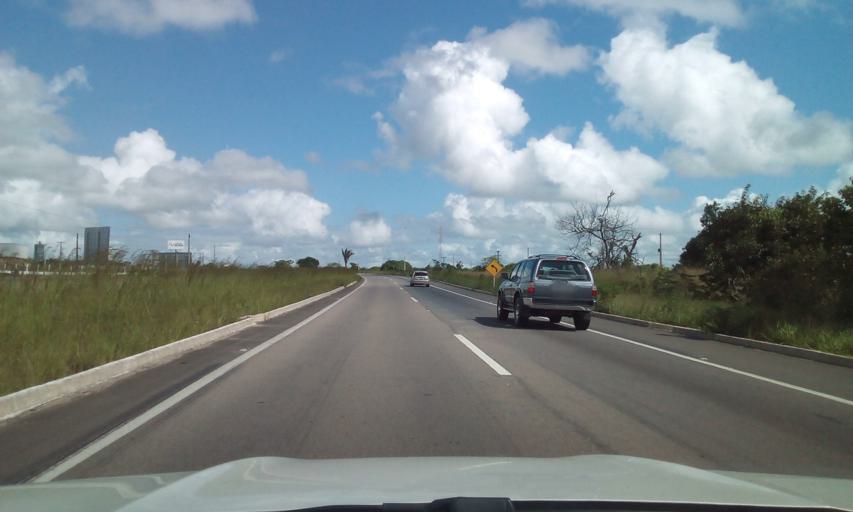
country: BR
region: Paraiba
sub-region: Conde
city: Conde
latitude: -7.2805
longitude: -34.9392
